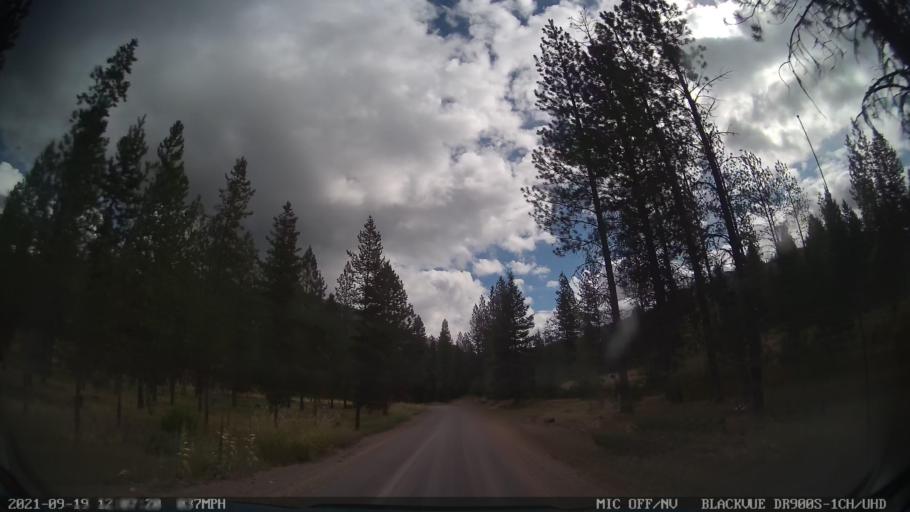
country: US
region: Montana
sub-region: Missoula County
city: Seeley Lake
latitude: 47.1841
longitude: -113.4082
